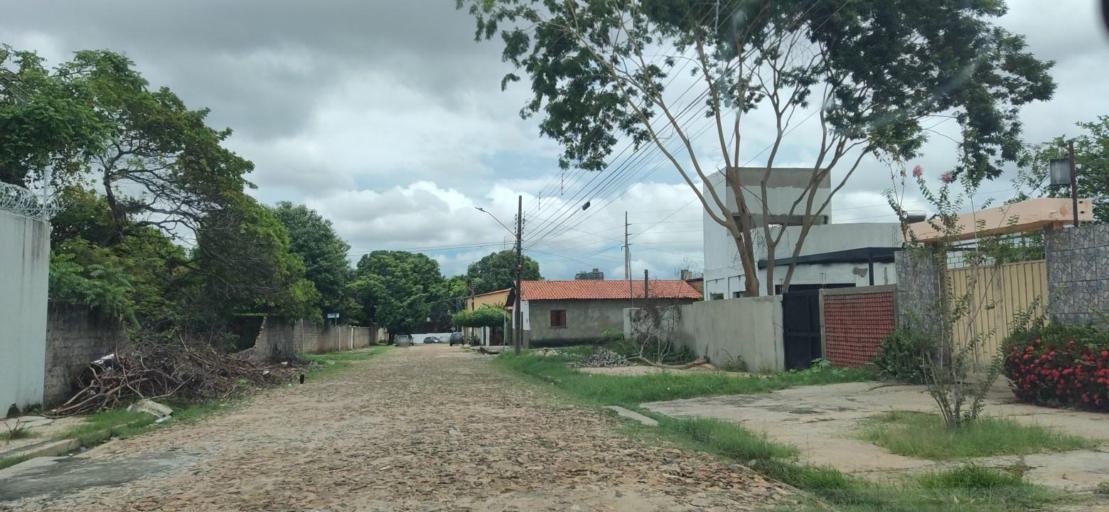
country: BR
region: Piaui
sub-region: Teresina
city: Teresina
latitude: -5.0753
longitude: -42.7642
